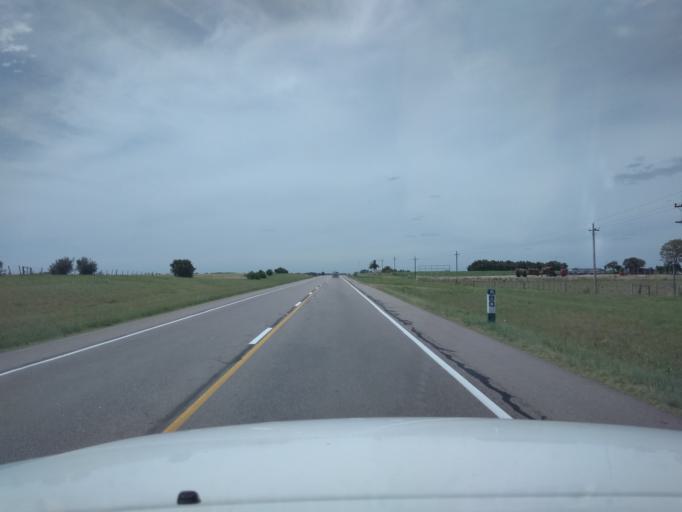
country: UY
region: Florida
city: Florida
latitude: -34.2289
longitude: -56.2120
